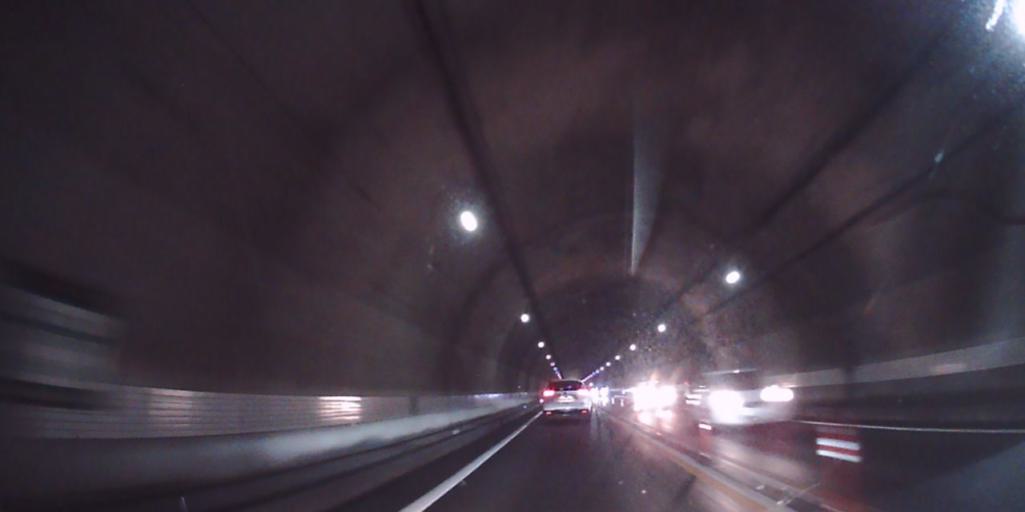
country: JP
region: Hokkaido
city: Niseko Town
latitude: 42.5935
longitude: 140.6761
